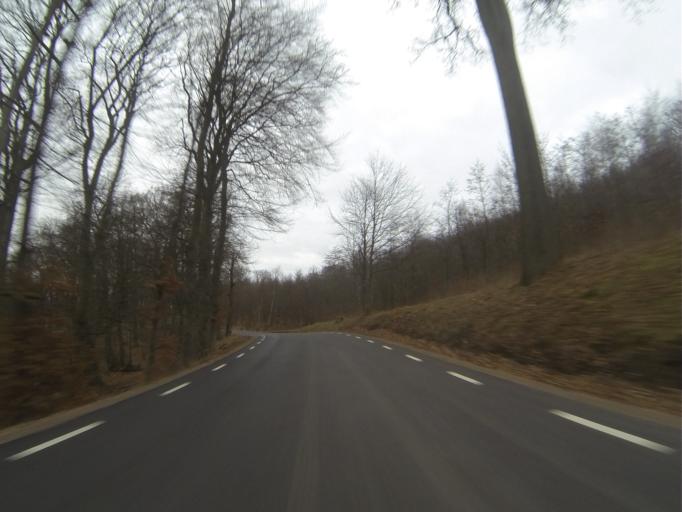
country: SE
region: Skane
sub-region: Lunds Kommun
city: Genarp
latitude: 55.5760
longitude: 13.4322
